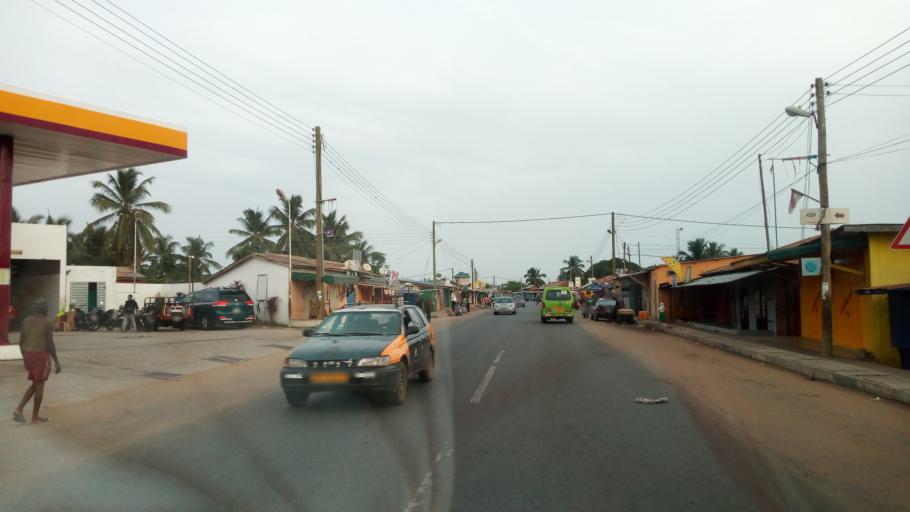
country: TG
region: Maritime
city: Lome
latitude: 6.1191
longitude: 1.1884
